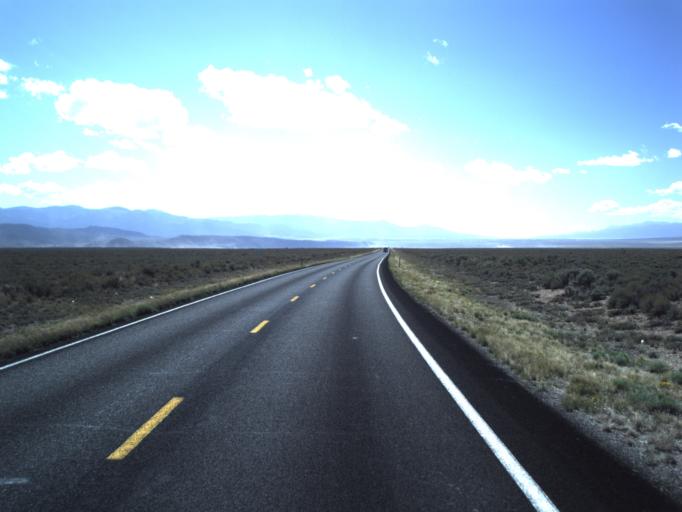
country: US
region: Utah
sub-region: Iron County
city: Enoch
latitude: 38.0018
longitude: -112.9980
